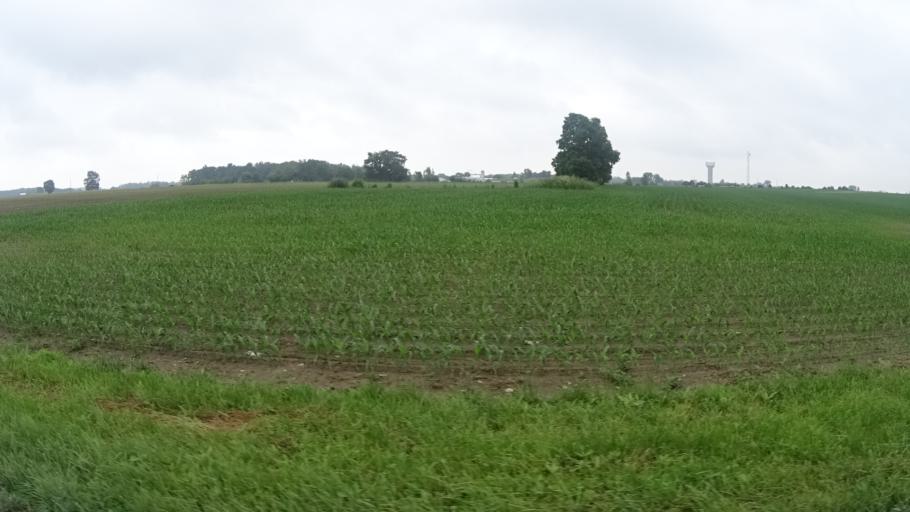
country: US
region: Ohio
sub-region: Huron County
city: Bellevue
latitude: 41.3474
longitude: -82.7607
